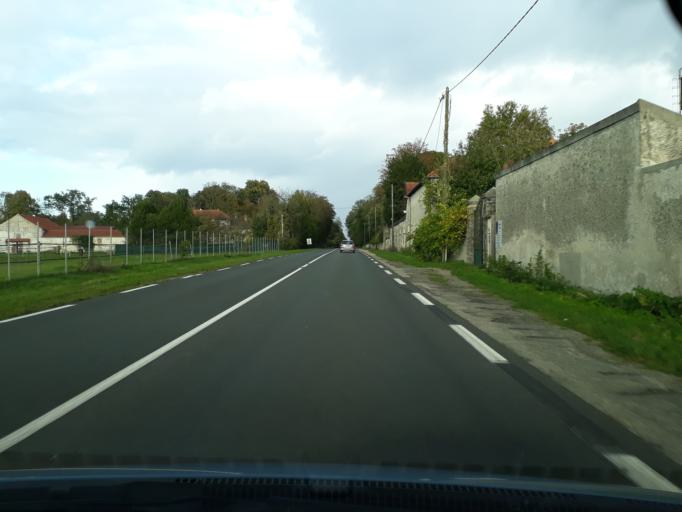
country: FR
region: Ile-de-France
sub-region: Departement de Seine-et-Marne
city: Acheres-la-Foret
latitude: 48.3493
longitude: 2.6102
